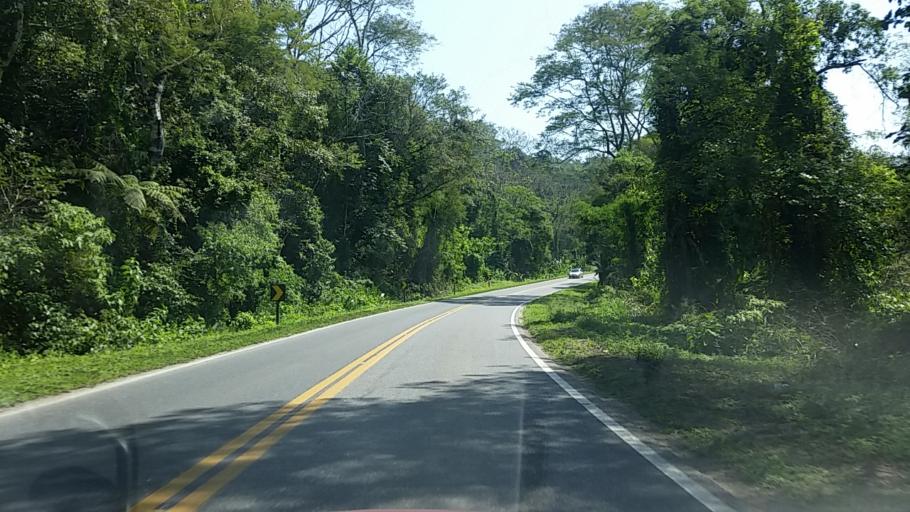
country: BR
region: Sao Paulo
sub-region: Miracatu
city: Miracatu
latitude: -24.3315
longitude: -47.5056
